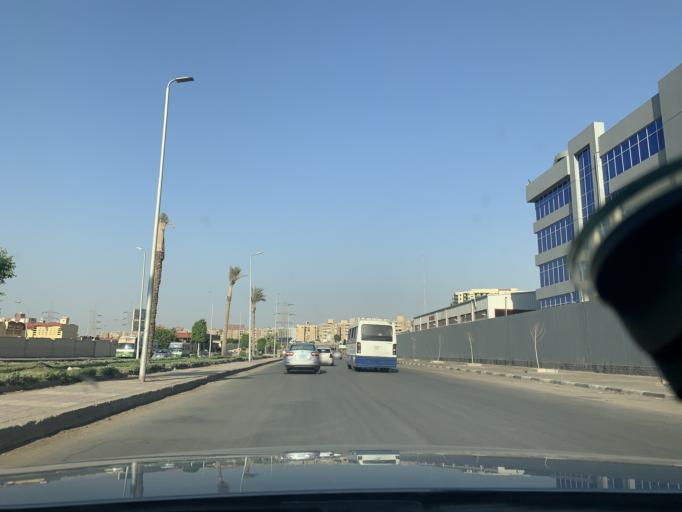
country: EG
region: Muhafazat al Qahirah
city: Cairo
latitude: 30.0354
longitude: 31.3511
